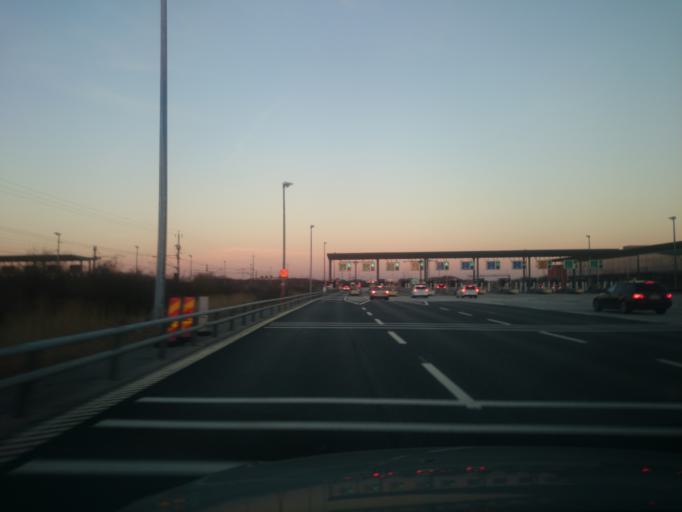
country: SE
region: Skane
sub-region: Malmo
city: Bunkeflostrand
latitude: 55.5656
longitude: 12.9107
